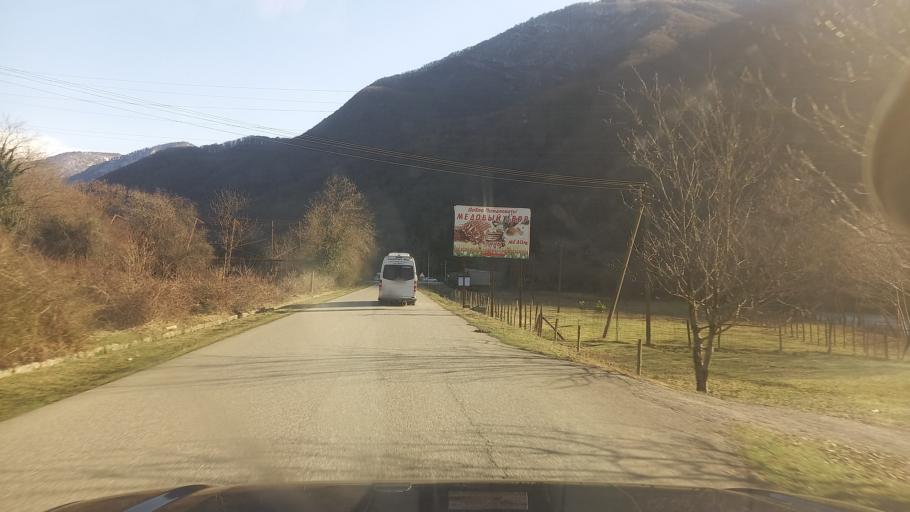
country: GE
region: Abkhazia
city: Gagra
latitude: 43.2817
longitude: 40.3962
